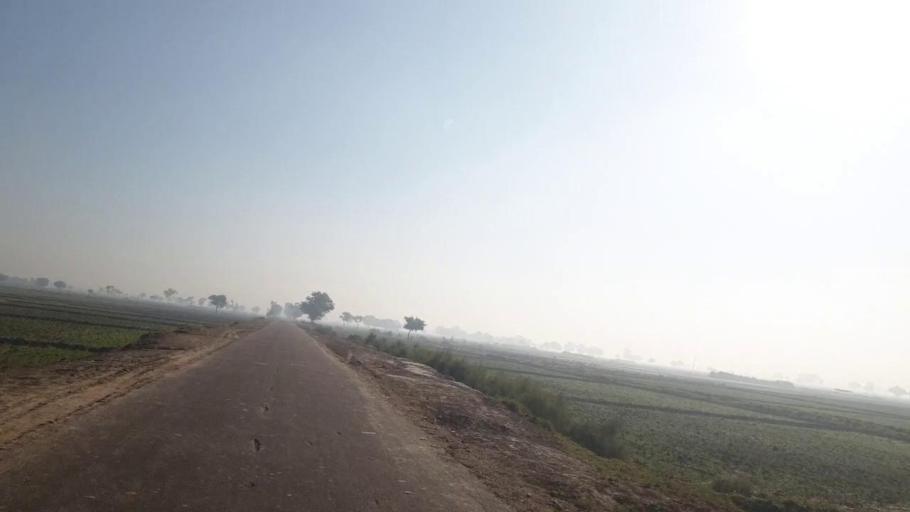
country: PK
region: Sindh
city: Dadu
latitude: 26.6732
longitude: 67.8159
